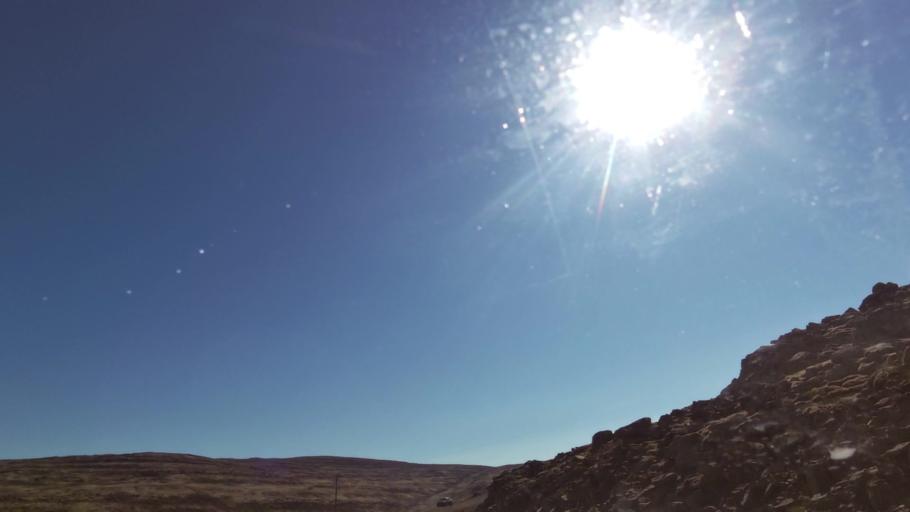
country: IS
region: West
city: Olafsvik
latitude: 65.5522
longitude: -24.2037
